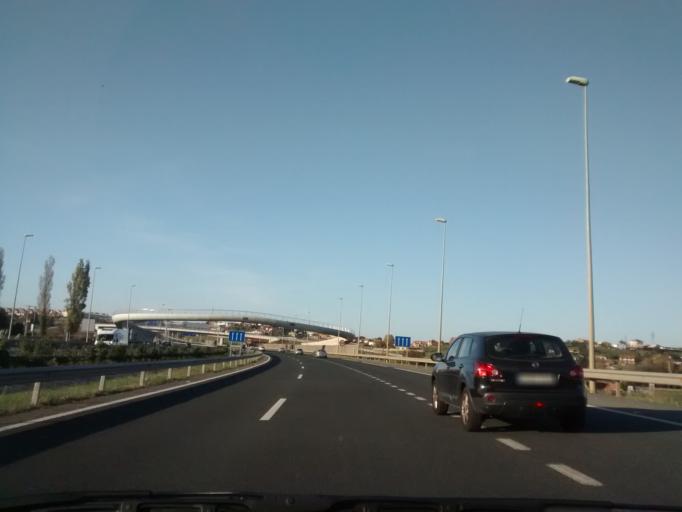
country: ES
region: Cantabria
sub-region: Provincia de Cantabria
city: Camargo
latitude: 43.4237
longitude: -3.8713
